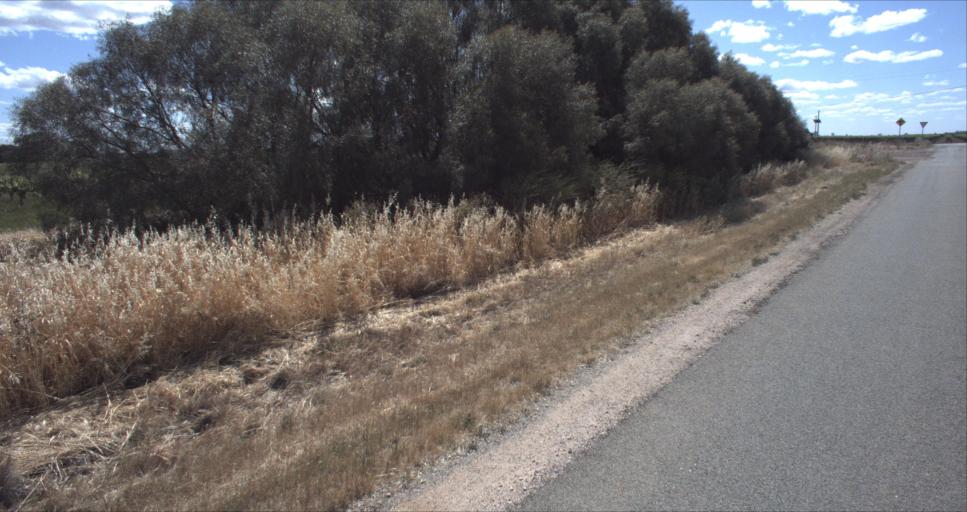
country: AU
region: New South Wales
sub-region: Leeton
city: Leeton
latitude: -34.5060
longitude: 146.2216
